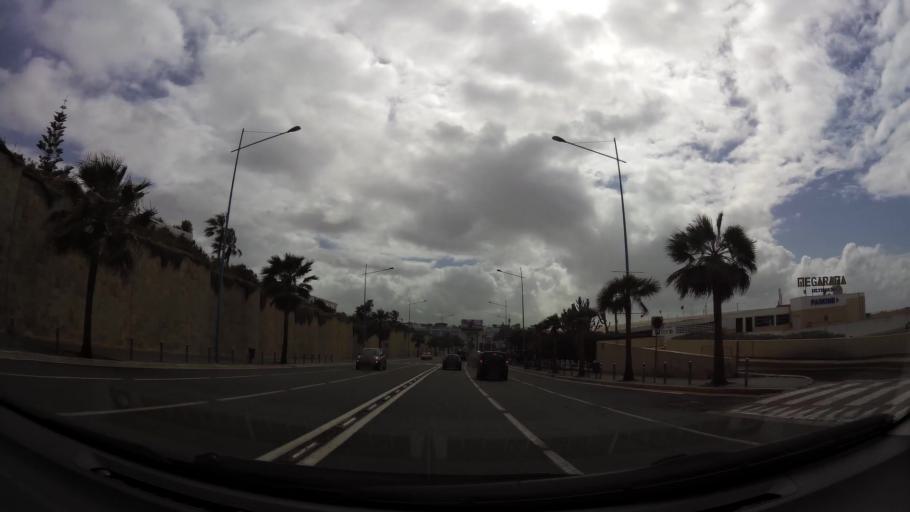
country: MA
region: Grand Casablanca
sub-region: Casablanca
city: Casablanca
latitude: 33.5967
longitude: -7.6664
